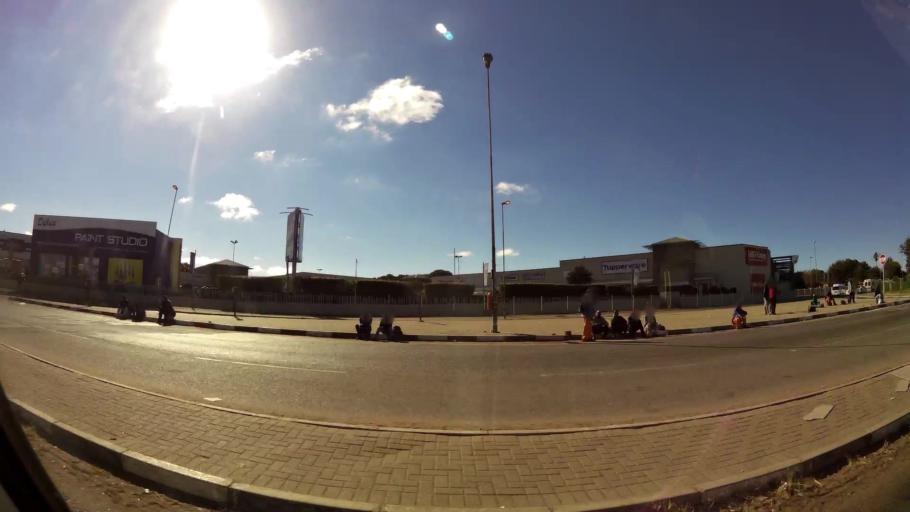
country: ZA
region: Limpopo
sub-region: Capricorn District Municipality
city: Polokwane
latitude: -23.8958
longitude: 29.4485
